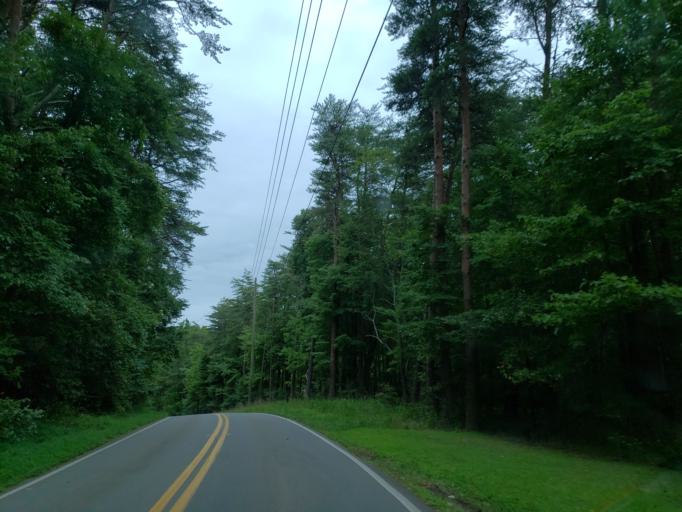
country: US
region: Georgia
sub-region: Pickens County
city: Jasper
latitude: 34.4235
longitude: -84.5414
